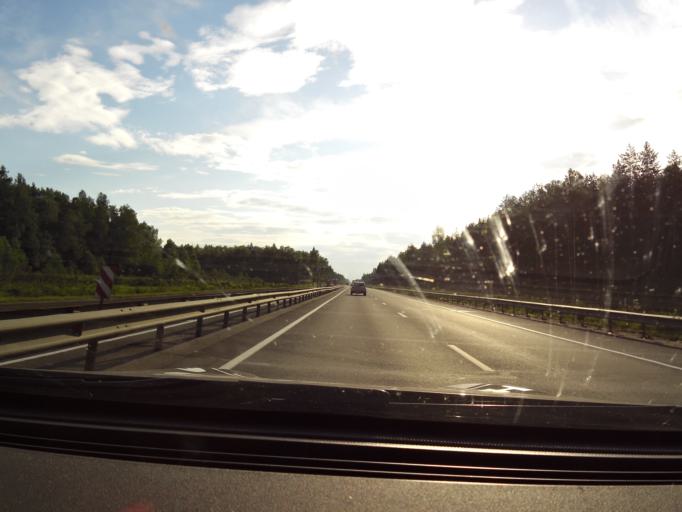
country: RU
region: Vladimir
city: Melekhovo
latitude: 56.2067
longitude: 41.2046
